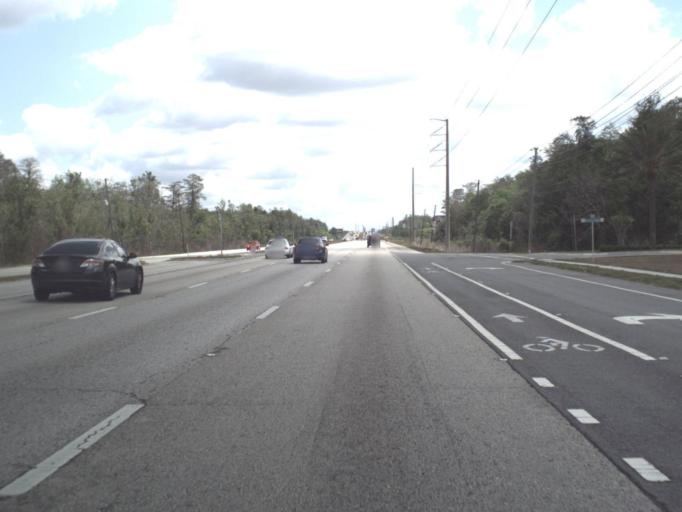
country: US
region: Florida
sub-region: Orange County
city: Sky Lake
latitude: 28.4508
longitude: -81.3806
